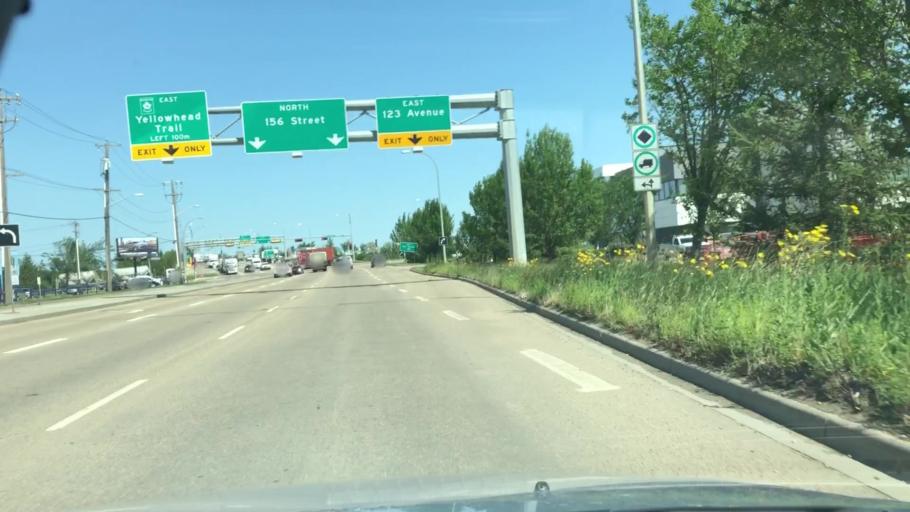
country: CA
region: Alberta
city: St. Albert
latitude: 53.5762
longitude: -113.5903
